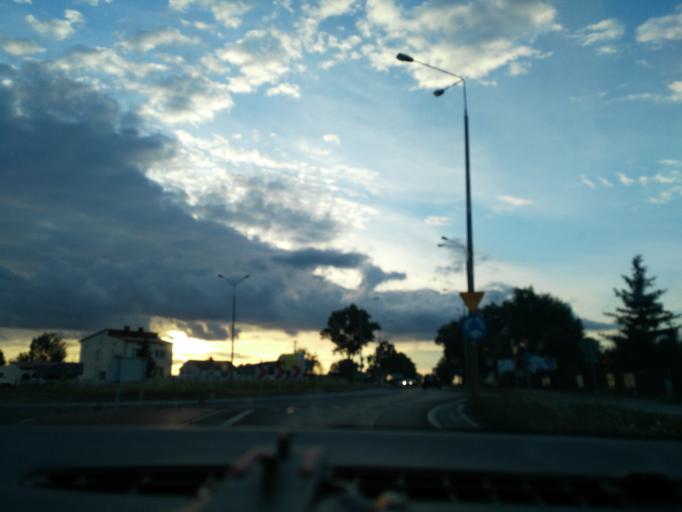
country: PL
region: Lublin Voivodeship
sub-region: Powiat lubartowski
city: Lubartow
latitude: 51.4359
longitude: 22.6253
